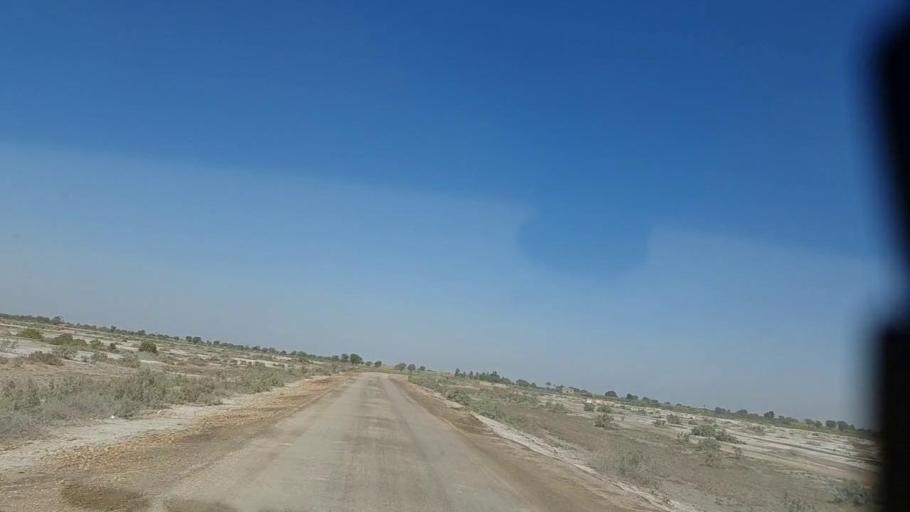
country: PK
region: Sindh
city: Digri
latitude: 25.1643
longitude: 69.0487
